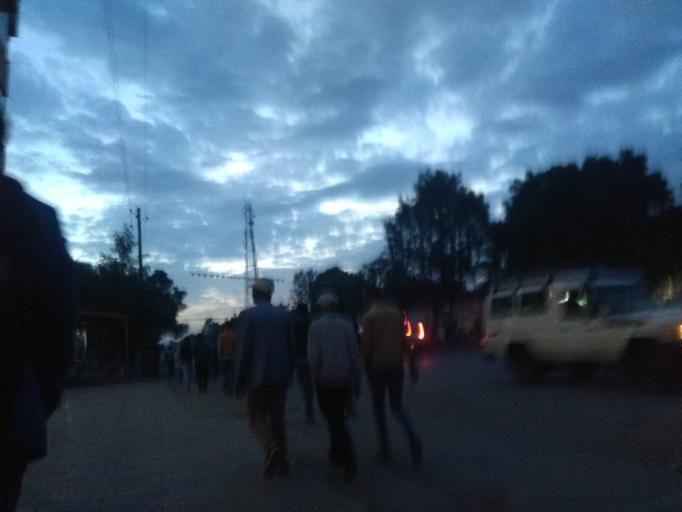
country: ET
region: Oromiya
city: Hagere Hiywet
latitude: 8.9819
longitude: 37.8532
